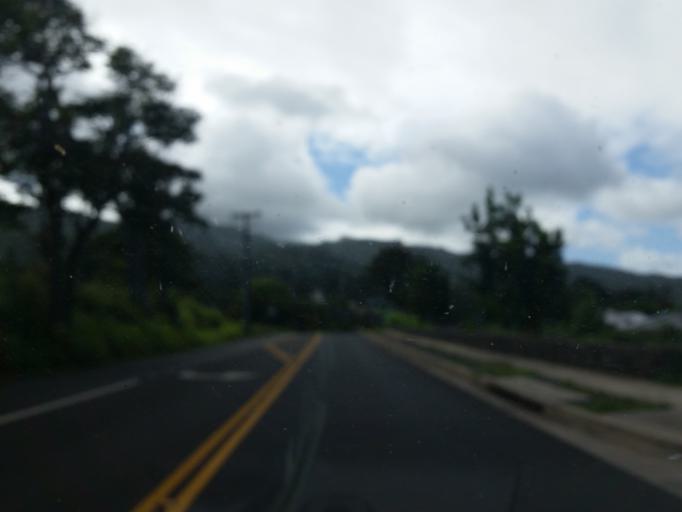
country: US
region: Hawaii
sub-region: Maui County
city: Waihee-Waiehu
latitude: 20.9286
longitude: -156.5091
